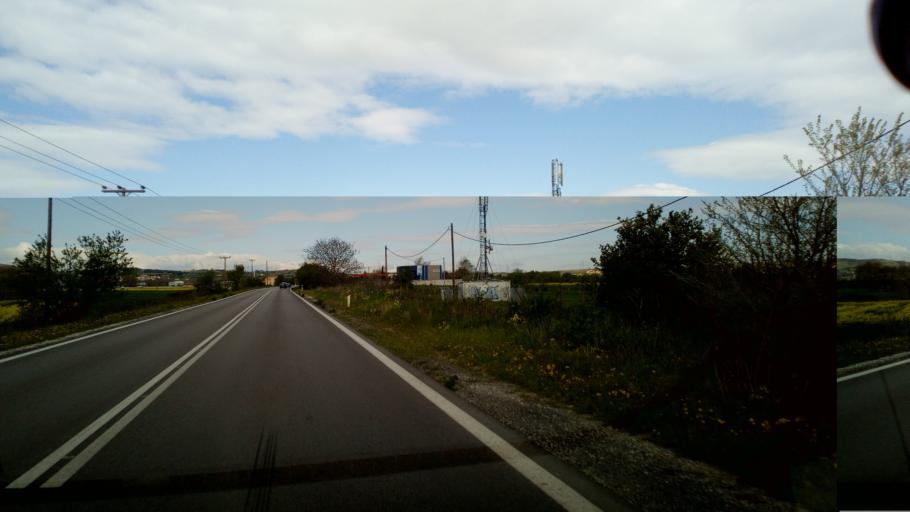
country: GR
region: Central Macedonia
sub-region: Nomos Thessalonikis
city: Drymos
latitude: 40.7647
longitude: 22.9604
